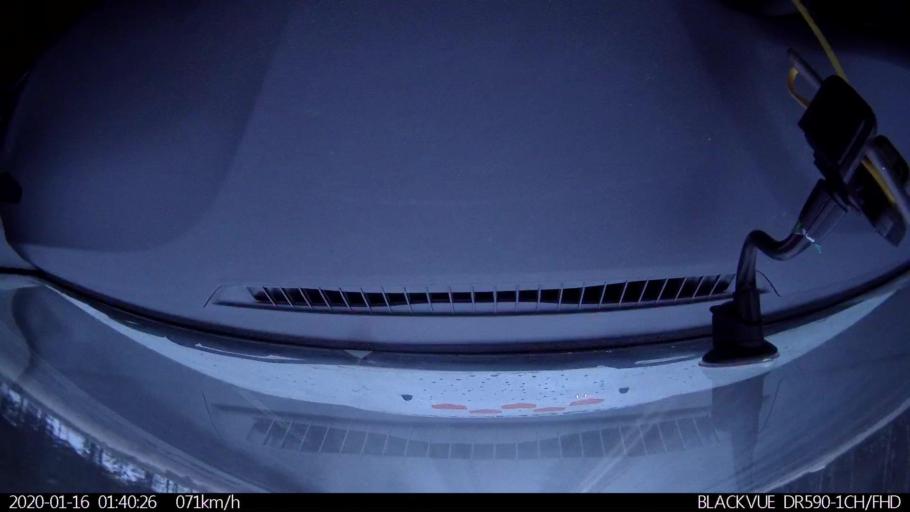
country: RU
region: Nizjnij Novgorod
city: Gorbatovka
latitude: 56.3267
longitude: 43.7797
